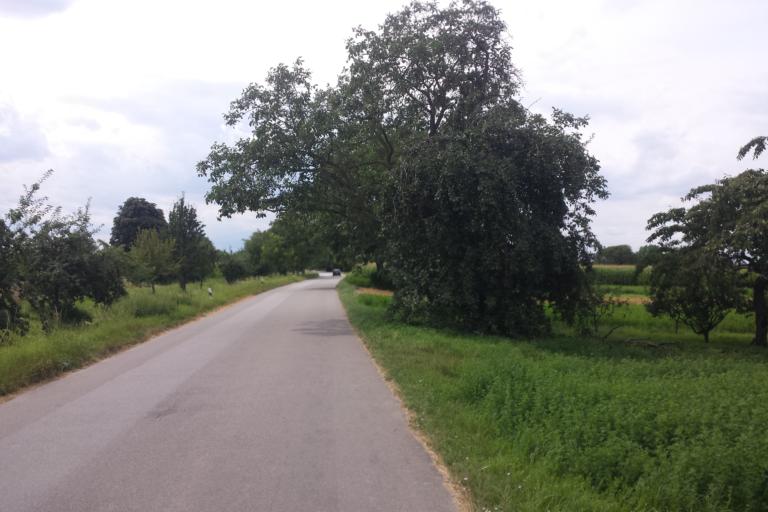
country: DE
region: Baden-Wuerttemberg
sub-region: Karlsruhe Region
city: Weinheim
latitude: 49.5590
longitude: 8.6418
